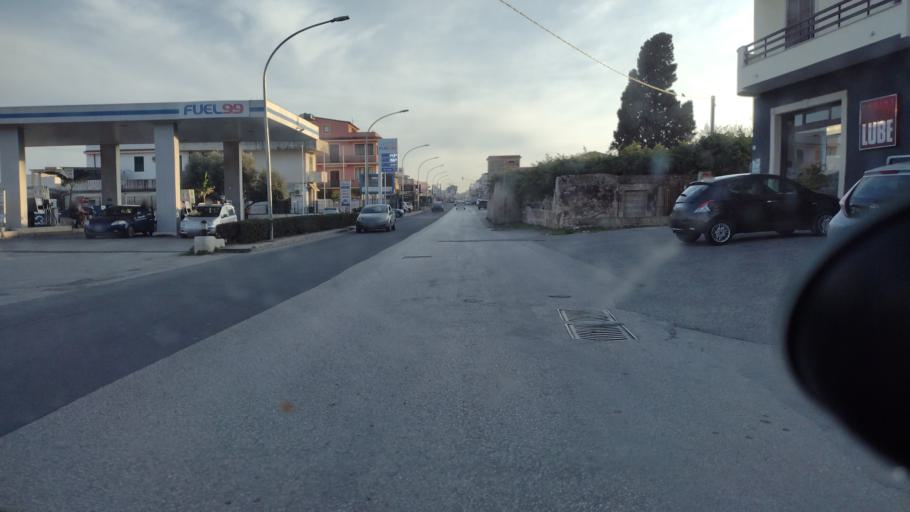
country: IT
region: Sicily
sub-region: Provincia di Siracusa
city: Avola
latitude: 36.9156
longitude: 15.1437
